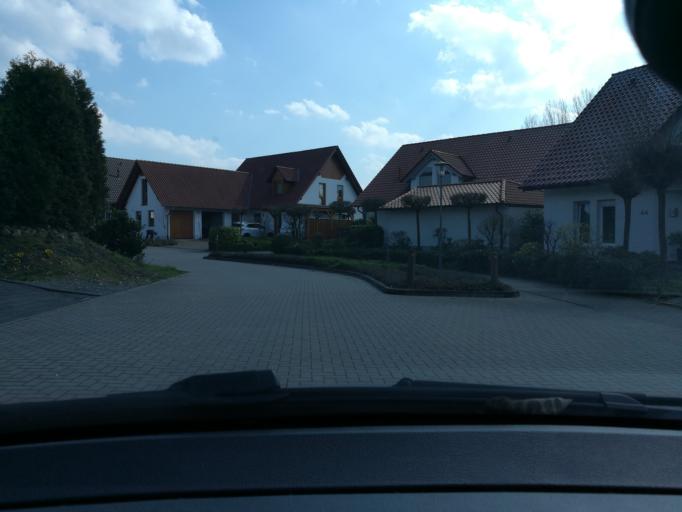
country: DE
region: North Rhine-Westphalia
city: Borgholzhausen
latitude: 52.0967
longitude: 8.3041
